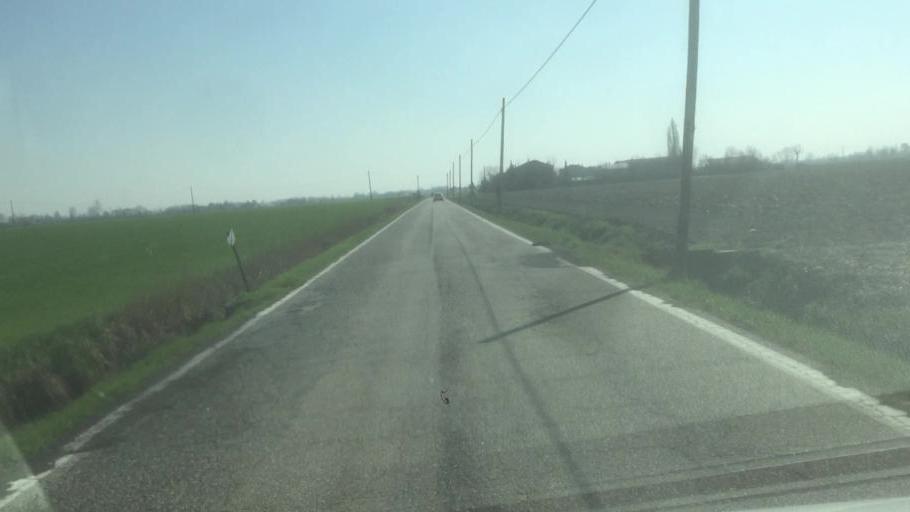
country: IT
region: Lombardy
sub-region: Provincia di Mantova
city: Ceresara
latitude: 45.2835
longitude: 10.5410
